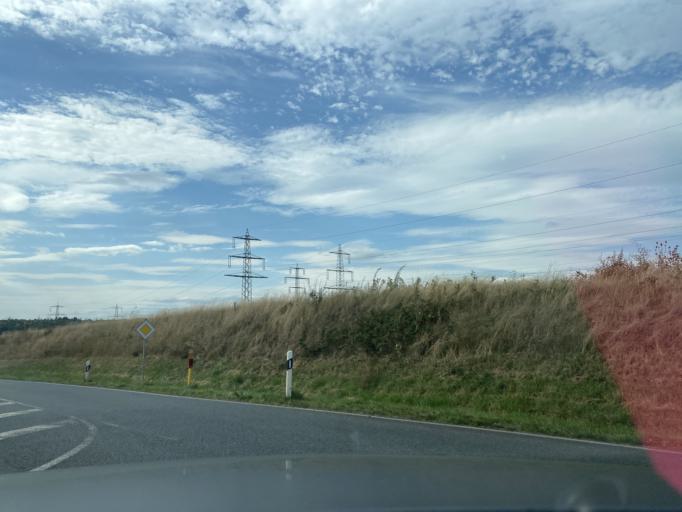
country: DE
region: Hesse
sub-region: Regierungsbezirk Darmstadt
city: Messel
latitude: 49.9752
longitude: 8.7428
